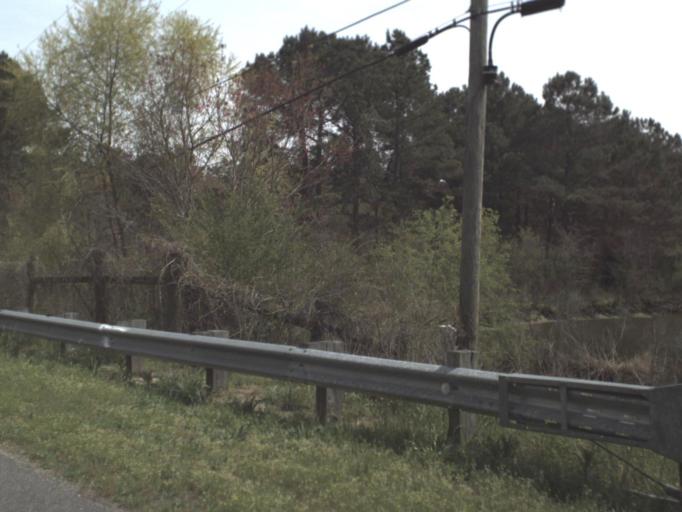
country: US
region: Florida
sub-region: Jackson County
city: Graceville
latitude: 30.9510
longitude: -85.4120
